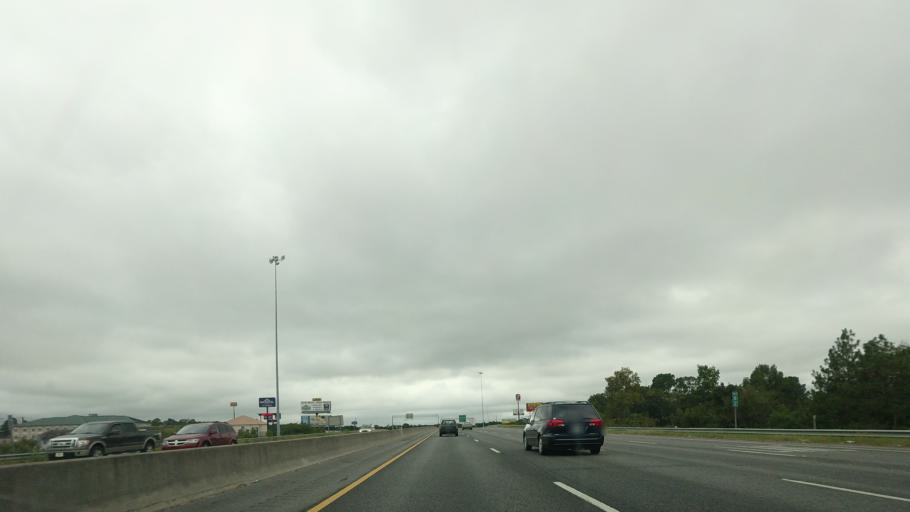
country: US
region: Georgia
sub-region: Tift County
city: Tifton
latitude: 31.4536
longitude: -83.5306
